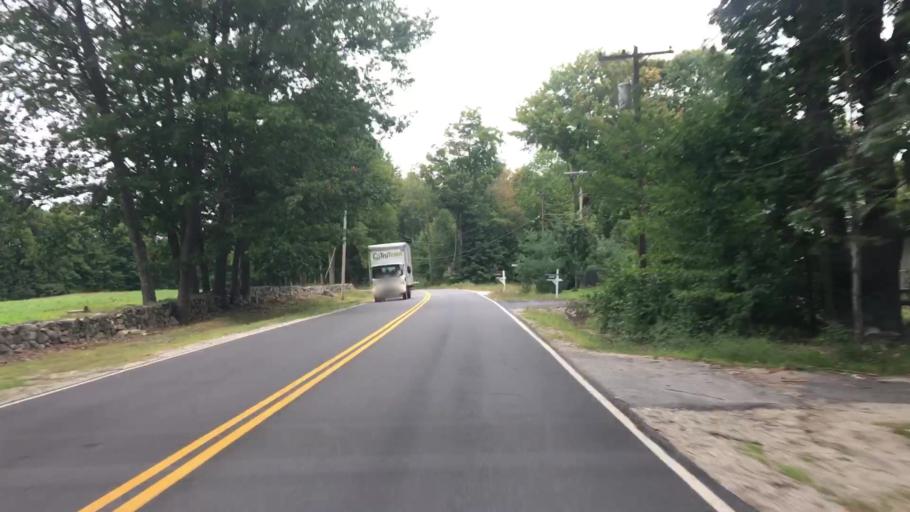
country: US
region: Maine
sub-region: Cumberland County
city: New Gloucester
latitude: 43.9080
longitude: -70.2503
